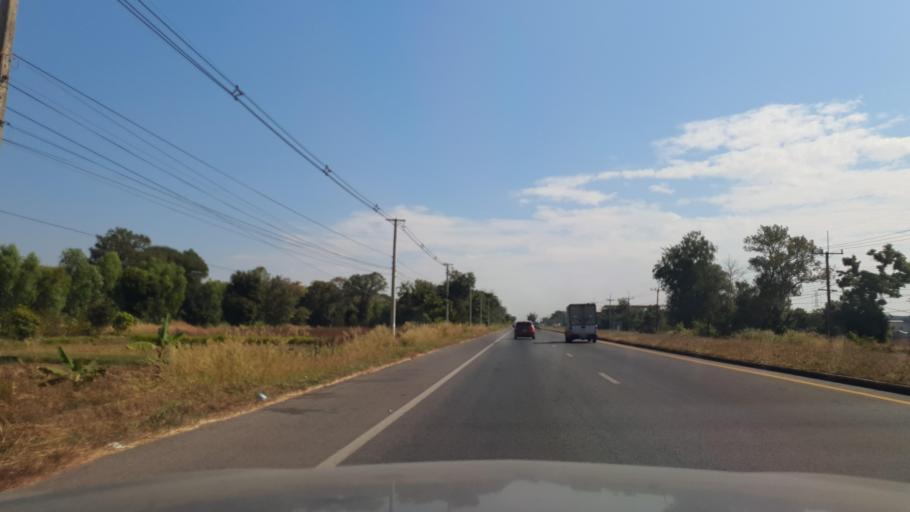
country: TH
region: Maha Sarakham
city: Chiang Yuen
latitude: 16.3734
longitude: 103.1492
